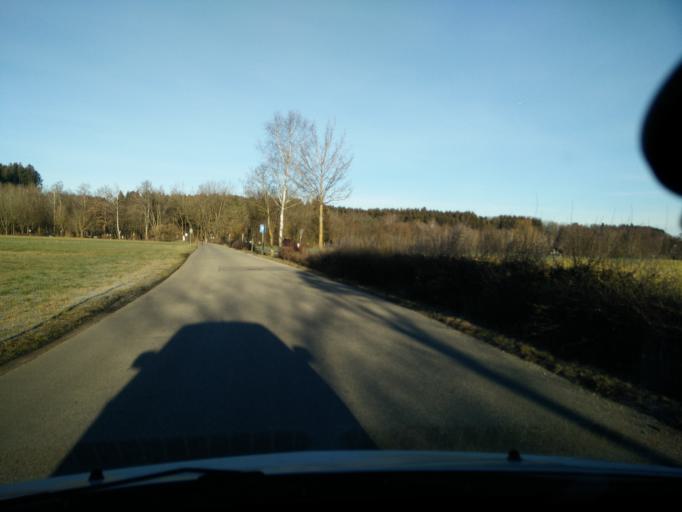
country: DE
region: Bavaria
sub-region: Upper Bavaria
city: Puchheim
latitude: 48.1332
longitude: 11.3440
